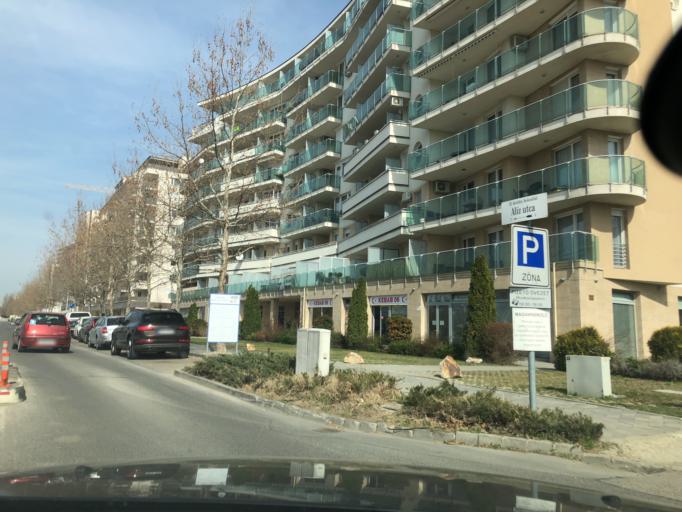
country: HU
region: Budapest
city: Budapest XI. keruelet
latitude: 47.4572
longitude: 19.0478
